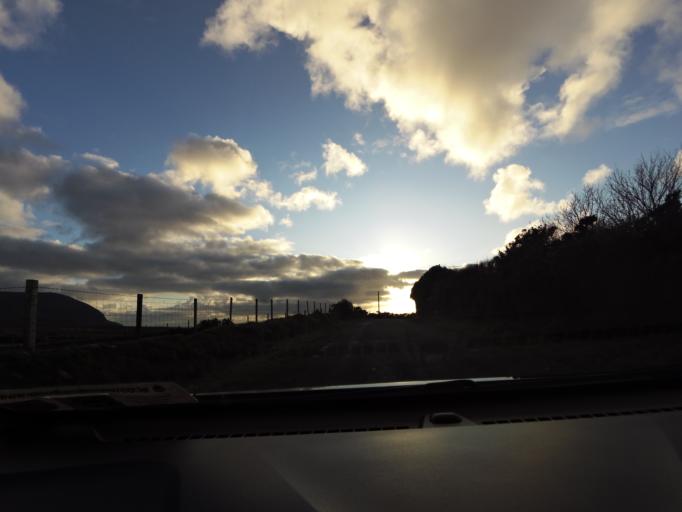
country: IE
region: Connaught
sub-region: Maigh Eo
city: Belmullet
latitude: 54.0005
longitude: -10.0322
